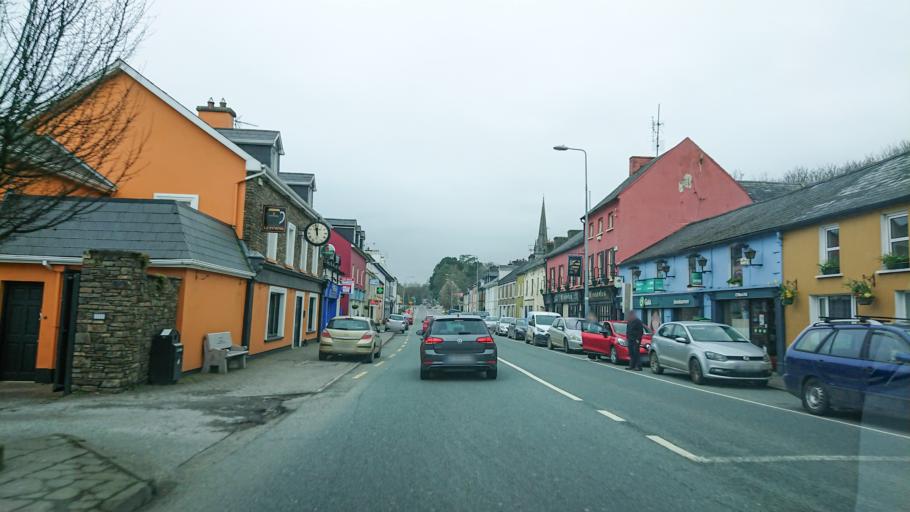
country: IE
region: Munster
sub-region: County Cork
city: Bandon
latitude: 51.7649
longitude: -8.6575
